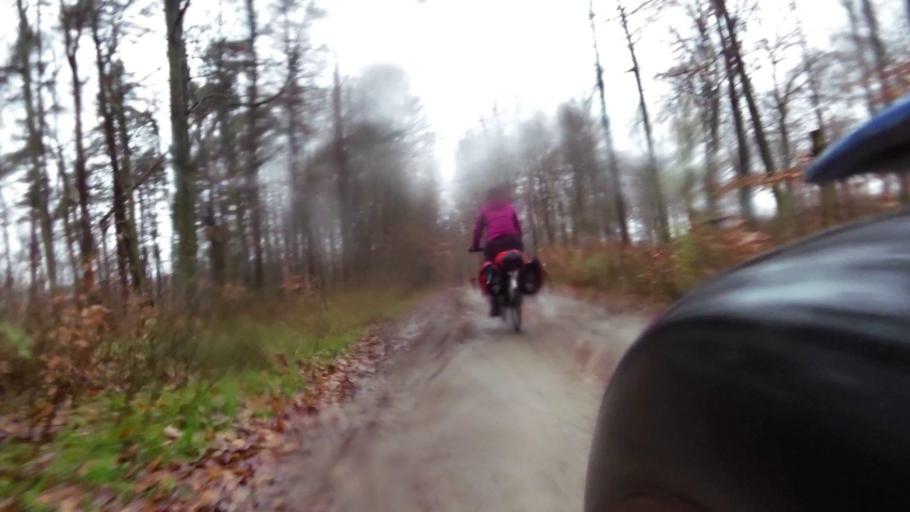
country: PL
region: West Pomeranian Voivodeship
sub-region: Powiat drawski
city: Czaplinek
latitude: 53.5164
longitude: 16.2006
